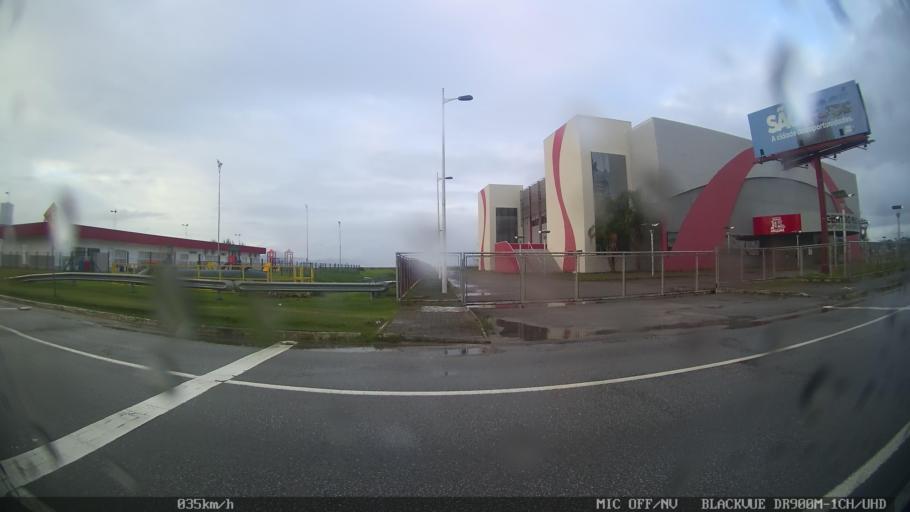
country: BR
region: Santa Catarina
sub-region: Sao Jose
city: Campinas
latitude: -27.6013
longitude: -48.6078
